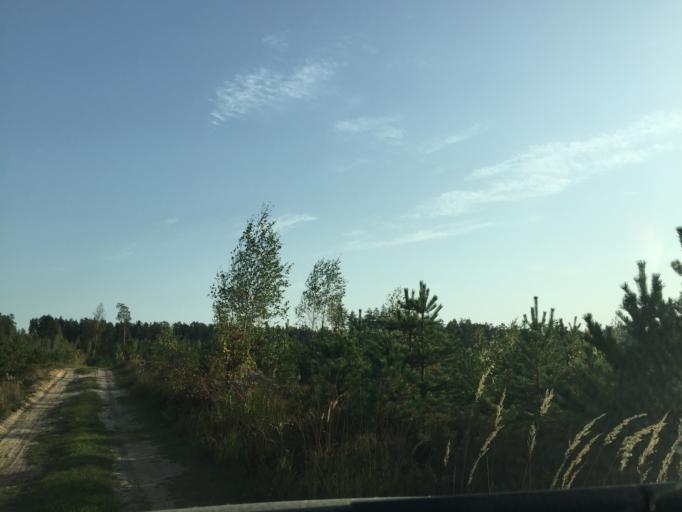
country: LV
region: Garkalne
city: Garkalne
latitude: 56.9689
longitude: 24.4202
